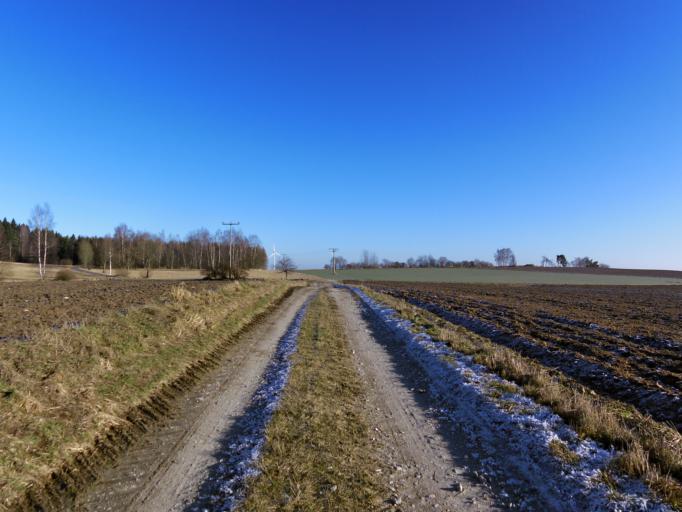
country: DE
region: Bavaria
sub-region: Upper Franconia
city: Hochstadt bei Thiersheim
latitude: 50.0768
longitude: 12.0461
